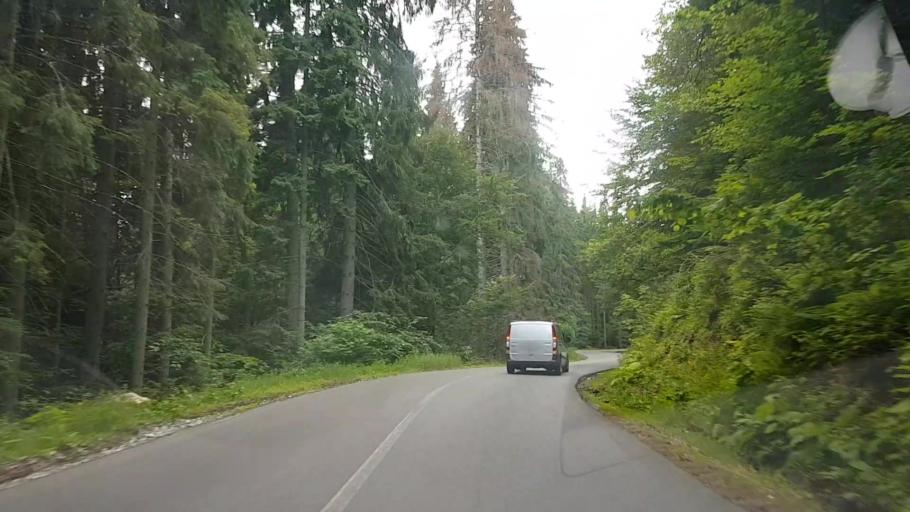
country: RO
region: Harghita
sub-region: Comuna Varsag
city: Varsag
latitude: 46.6711
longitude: 25.3253
